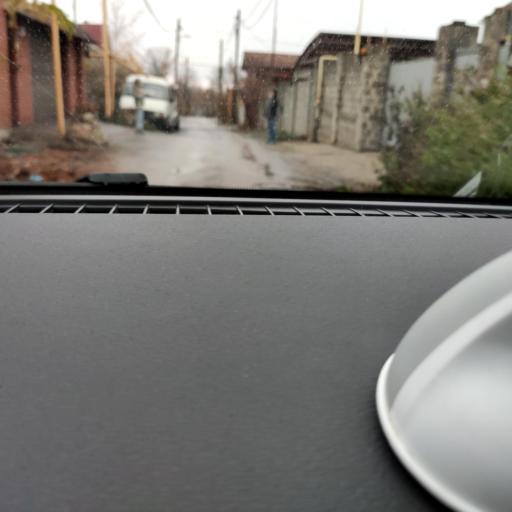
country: RU
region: Samara
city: Samara
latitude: 53.2714
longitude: 50.2114
